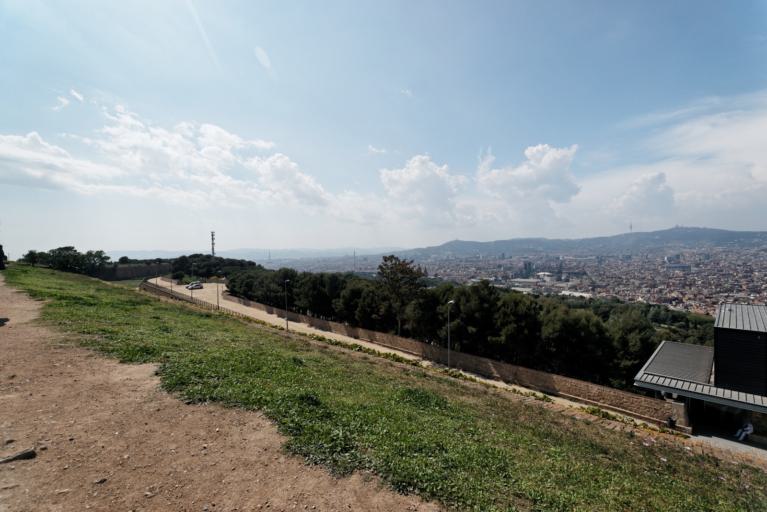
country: ES
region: Catalonia
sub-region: Provincia de Barcelona
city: Sants-Montjuic
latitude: 41.3644
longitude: 2.1666
